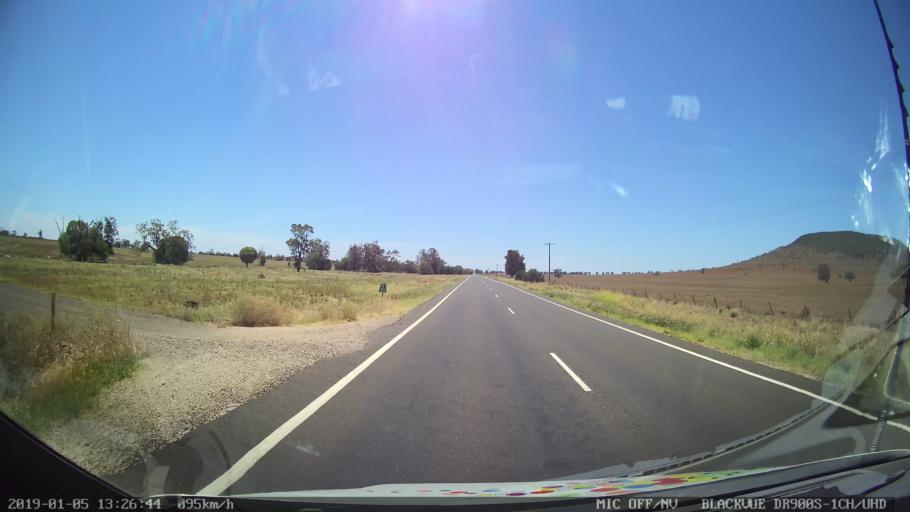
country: AU
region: New South Wales
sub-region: Gunnedah
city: Gunnedah
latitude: -31.0505
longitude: 150.0196
